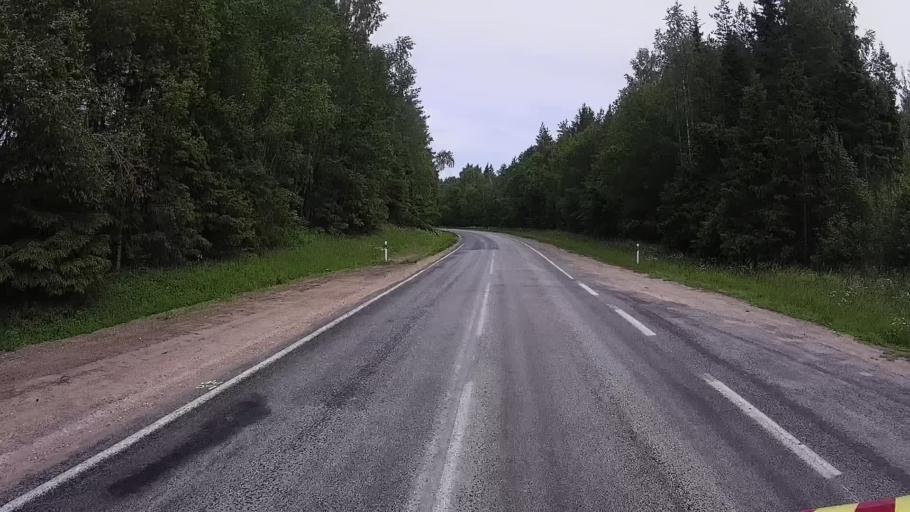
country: EE
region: Viljandimaa
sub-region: Karksi vald
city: Karksi-Nuia
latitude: 58.2092
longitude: 25.6212
